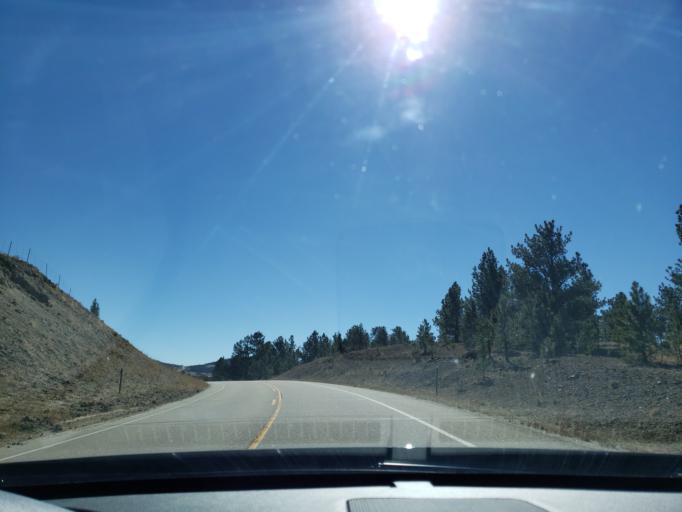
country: US
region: Colorado
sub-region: Chaffee County
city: Buena Vista
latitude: 38.8687
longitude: -105.6674
